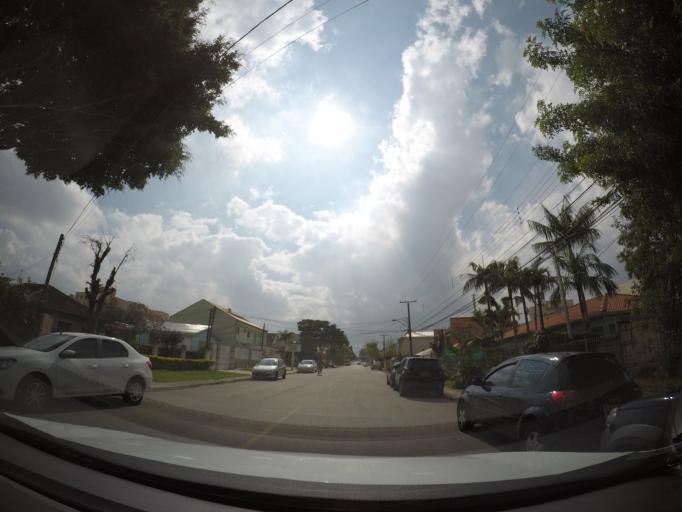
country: BR
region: Parana
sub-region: Sao Jose Dos Pinhais
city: Sao Jose dos Pinhais
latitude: -25.4859
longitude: -49.2491
